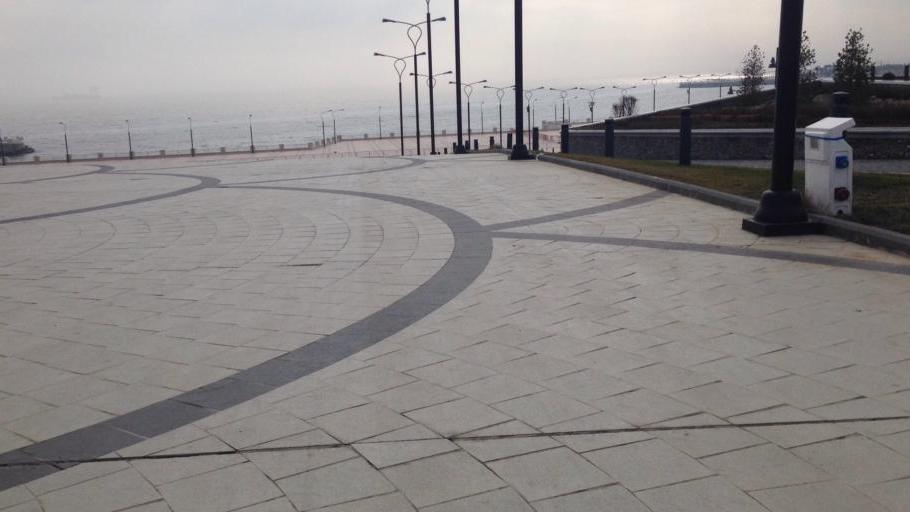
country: AZ
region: Baki
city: Badamdar
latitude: 40.3436
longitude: 49.8438
